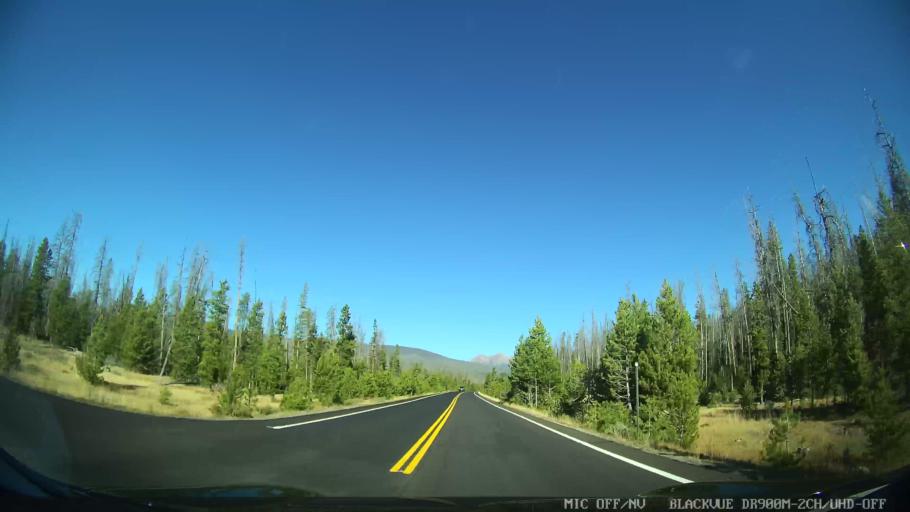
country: US
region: Colorado
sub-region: Grand County
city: Granby
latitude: 40.2822
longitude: -105.8379
